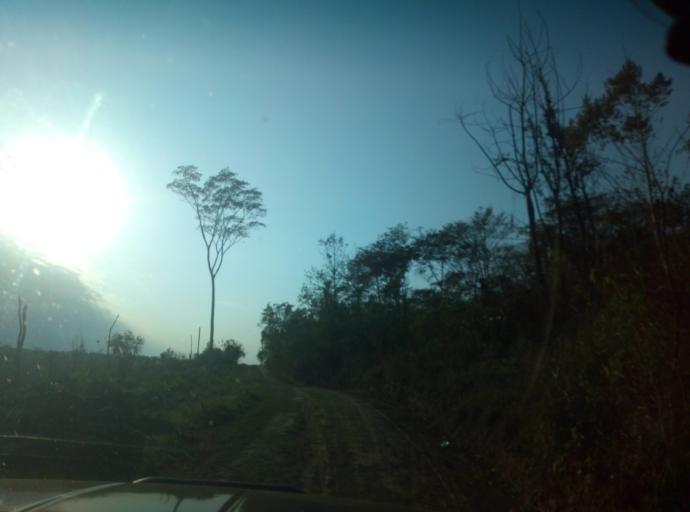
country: PY
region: Caaguazu
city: Doctor Cecilio Baez
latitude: -25.1986
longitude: -56.1313
